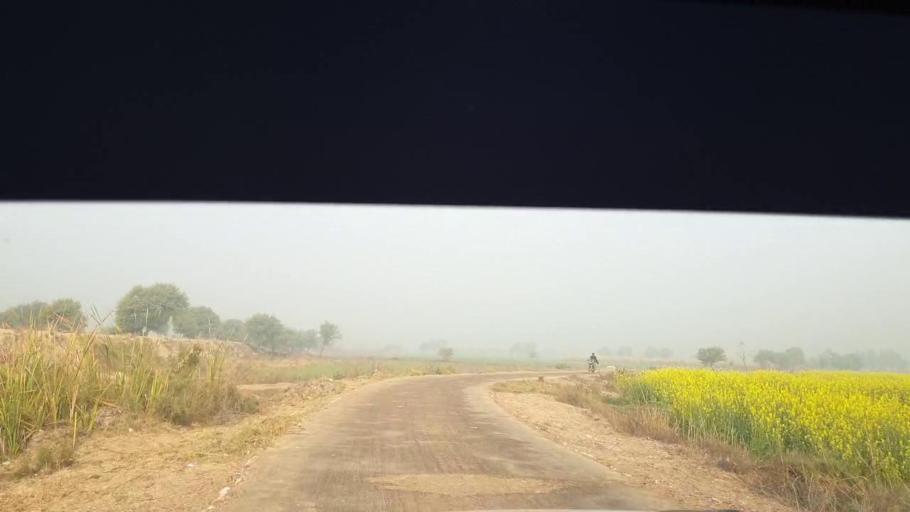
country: PK
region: Sindh
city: Berani
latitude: 25.7841
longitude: 68.7718
